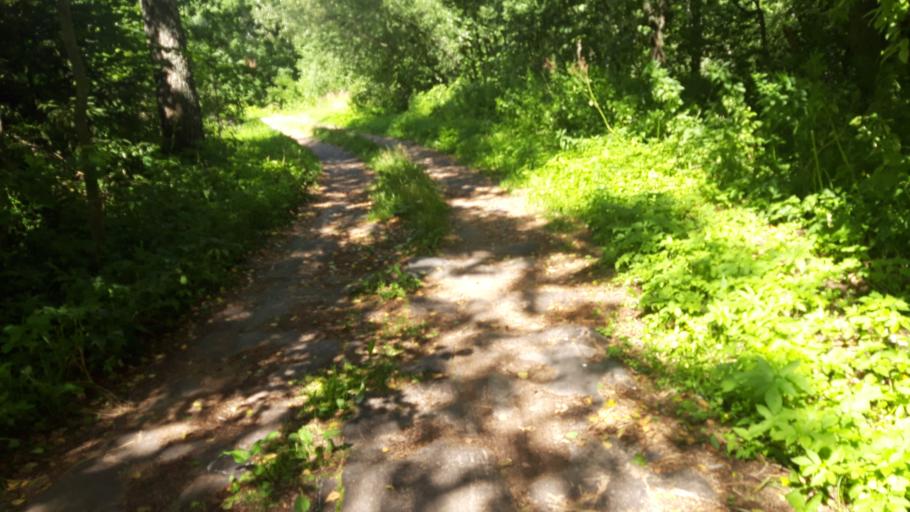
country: RU
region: Tverskaya
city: Konakovo
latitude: 56.6836
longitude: 36.6962
